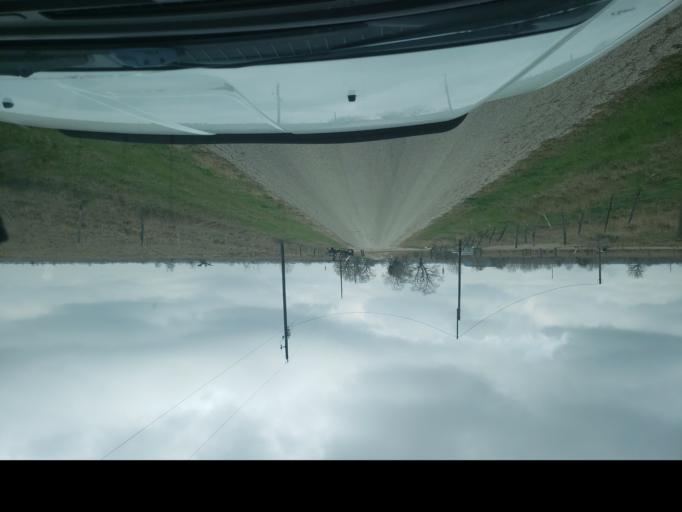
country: US
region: Texas
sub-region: Fort Bend County
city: Needville
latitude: 29.3494
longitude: -95.7547
